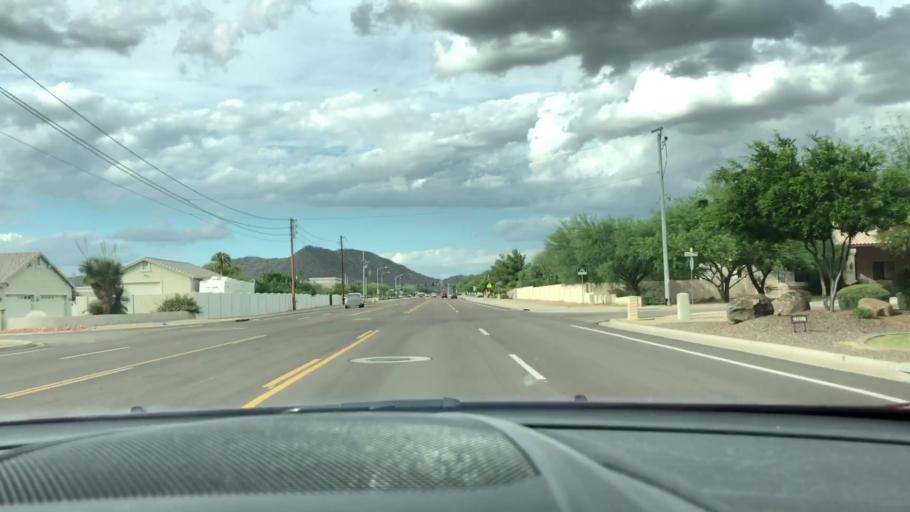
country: US
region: Arizona
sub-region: Maricopa County
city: Sun City
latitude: 33.6923
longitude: -112.2377
